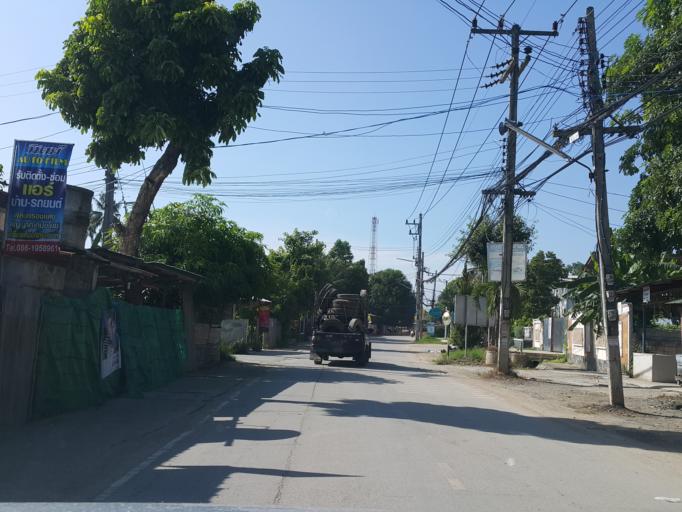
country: TH
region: Chiang Mai
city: Saraphi
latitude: 18.7602
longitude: 99.0539
